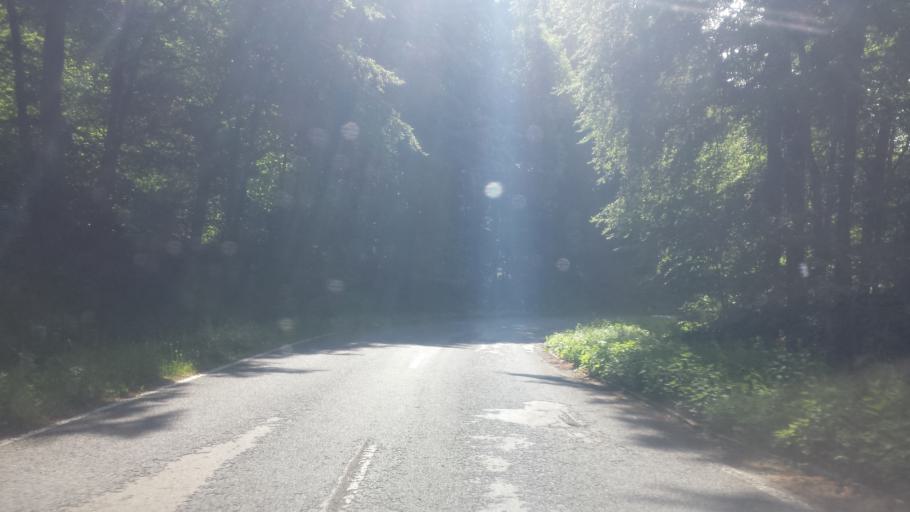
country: DE
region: Hesse
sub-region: Regierungsbezirk Darmstadt
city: Rimbach
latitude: 49.5857
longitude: 8.7829
